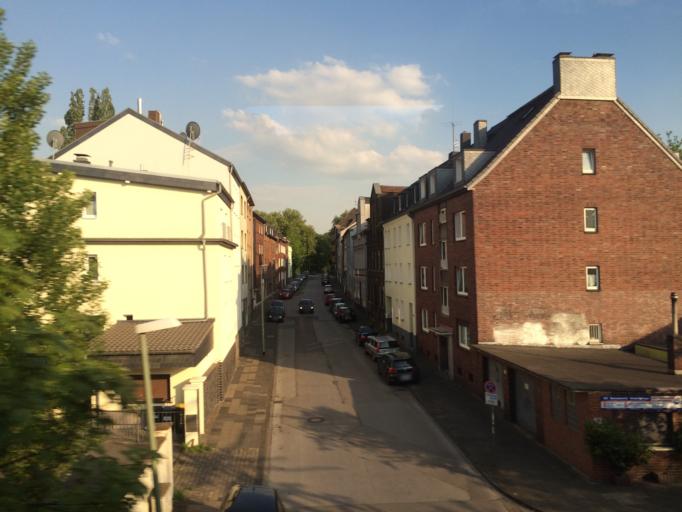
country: DE
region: North Rhine-Westphalia
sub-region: Regierungsbezirk Dusseldorf
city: Duisburg
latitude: 51.4410
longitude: 6.7924
